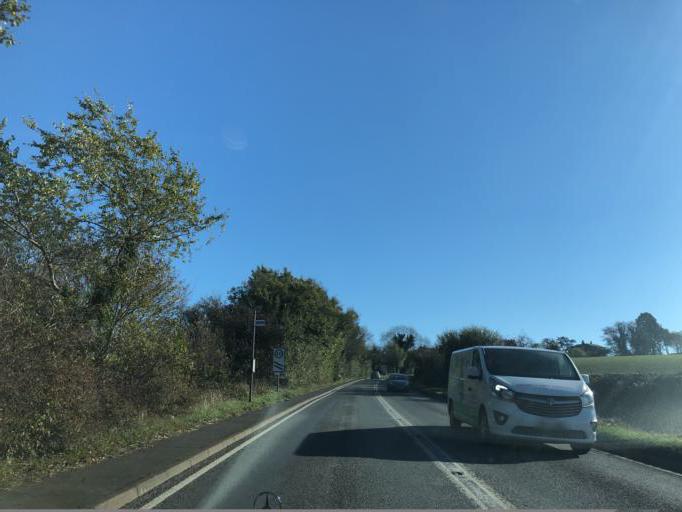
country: GB
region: England
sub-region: Warwickshire
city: Harbury
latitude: 52.2593
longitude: -1.4493
